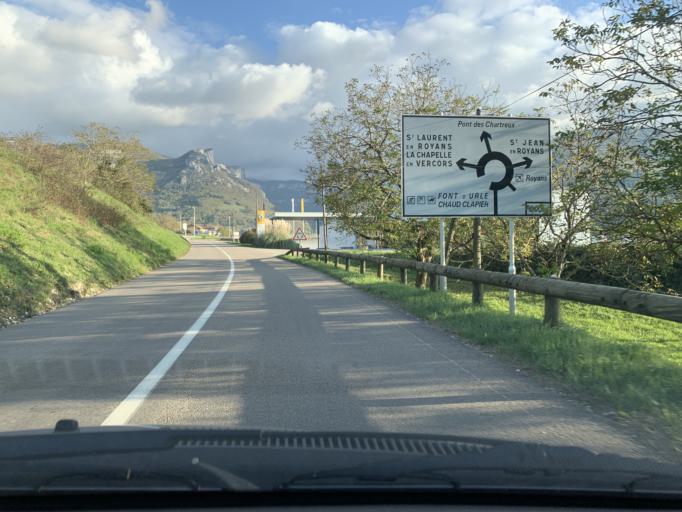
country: FR
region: Rhone-Alpes
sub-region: Departement de la Drome
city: Saint-Laurent-en-Royans
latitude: 45.0336
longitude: 5.3083
